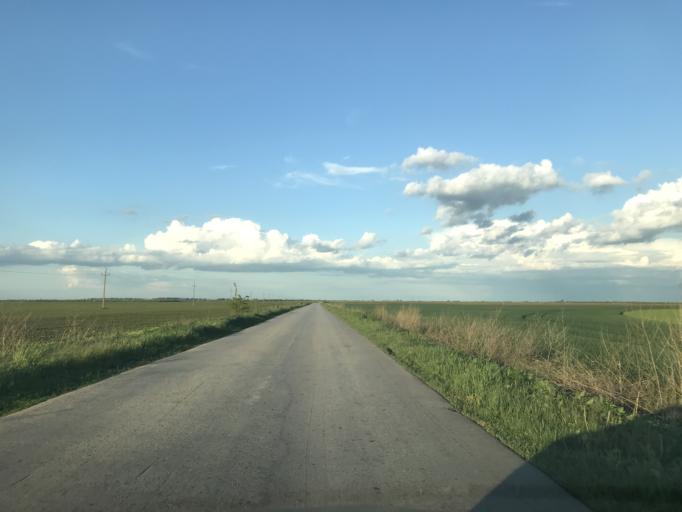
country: RS
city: Mihajlovo
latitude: 45.4491
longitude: 20.4009
